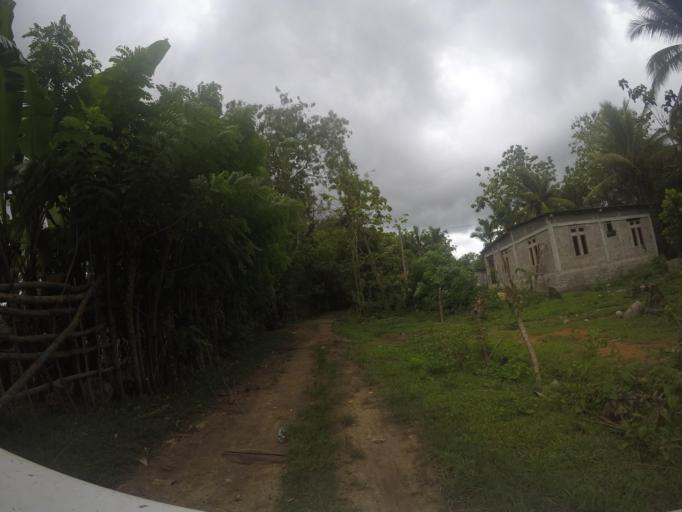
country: TL
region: Lautem
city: Lospalos
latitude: -8.5212
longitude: 126.9896
